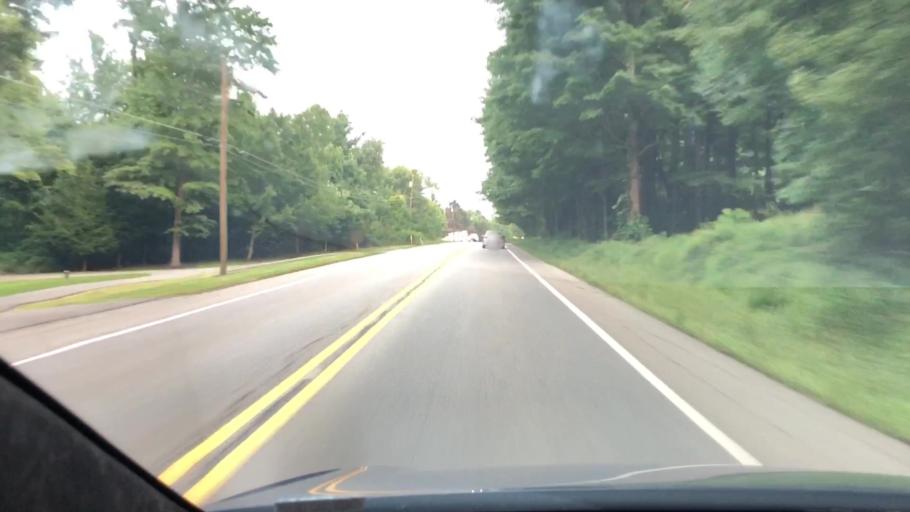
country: US
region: Pennsylvania
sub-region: Butler County
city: Slippery Rock
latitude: 40.9996
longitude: -79.9910
